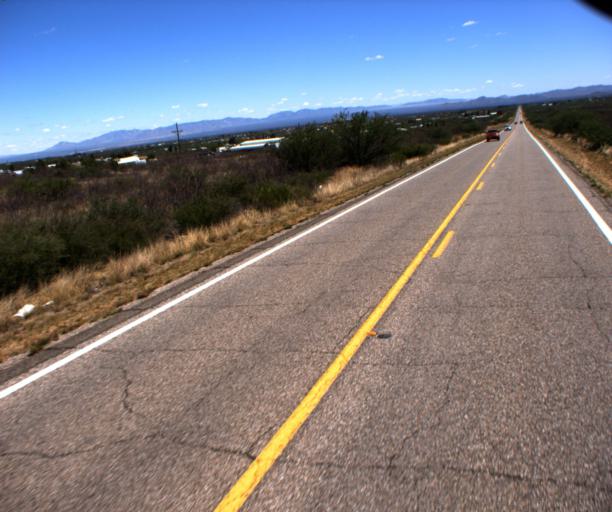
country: US
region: Arizona
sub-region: Cochise County
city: Huachuca City
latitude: 31.6919
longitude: -110.3871
